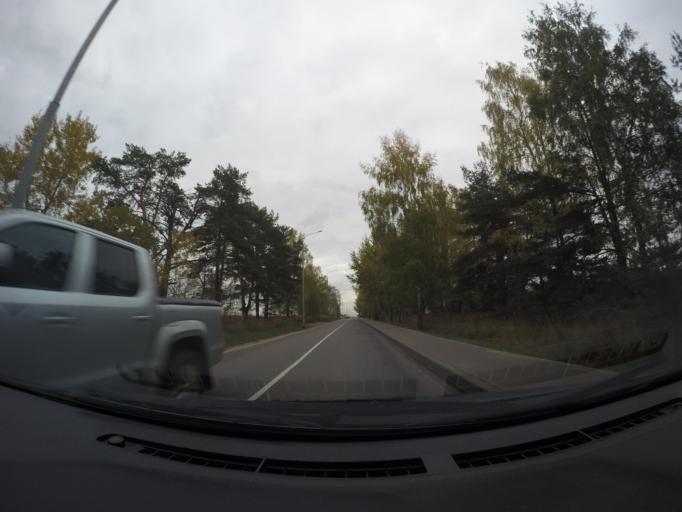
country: RU
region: Moskovskaya
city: Vishnyakovskiye Dachi
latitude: 55.8056
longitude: 38.1294
